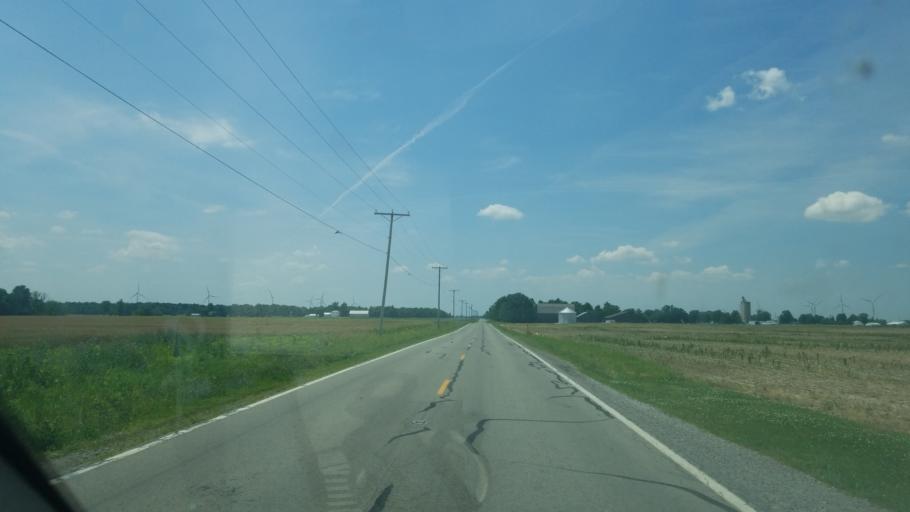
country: US
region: Ohio
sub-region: Hancock County
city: Arlington
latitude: 40.7797
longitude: -83.6781
